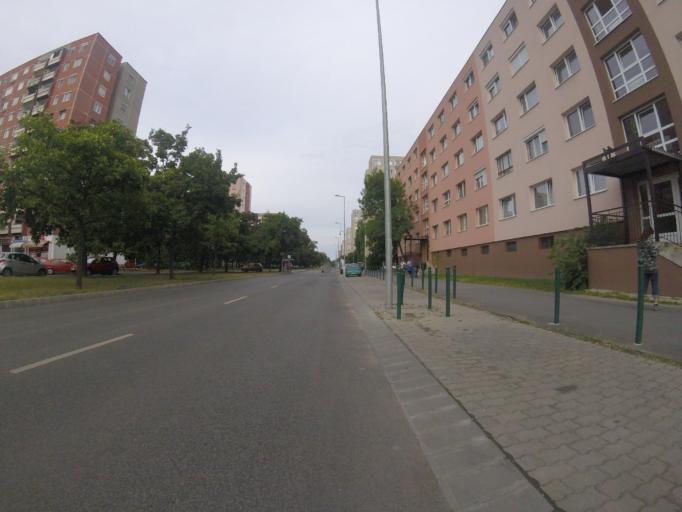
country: HU
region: Pest
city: Budakalasz
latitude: 47.5972
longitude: 19.0580
